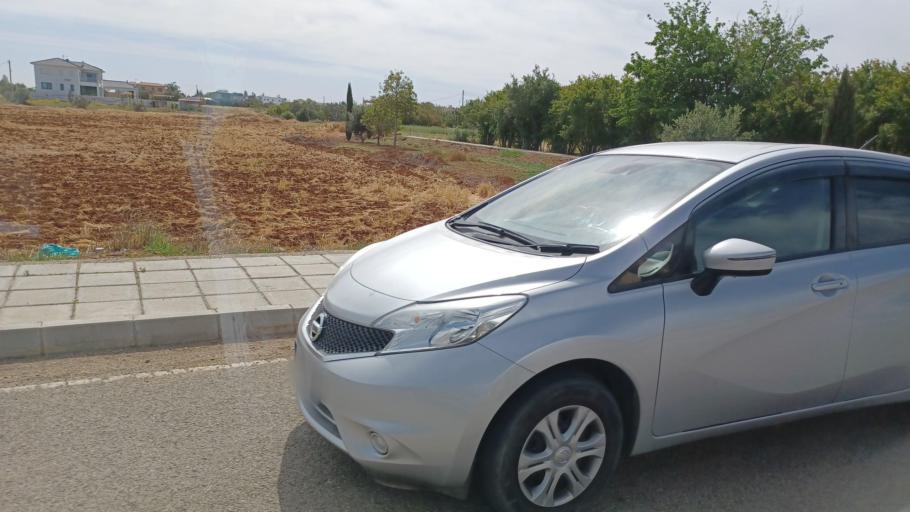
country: CY
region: Lefkosia
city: Kokkinotrimithia
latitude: 35.1506
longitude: 33.2064
